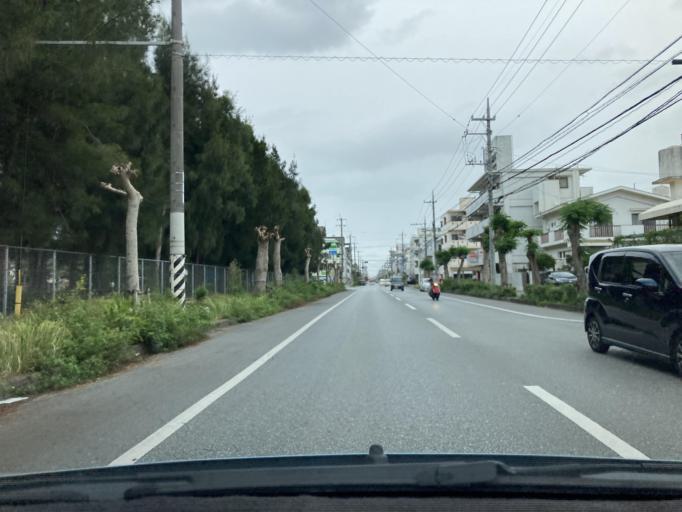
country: JP
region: Okinawa
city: Itoman
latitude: 26.1380
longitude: 127.6669
